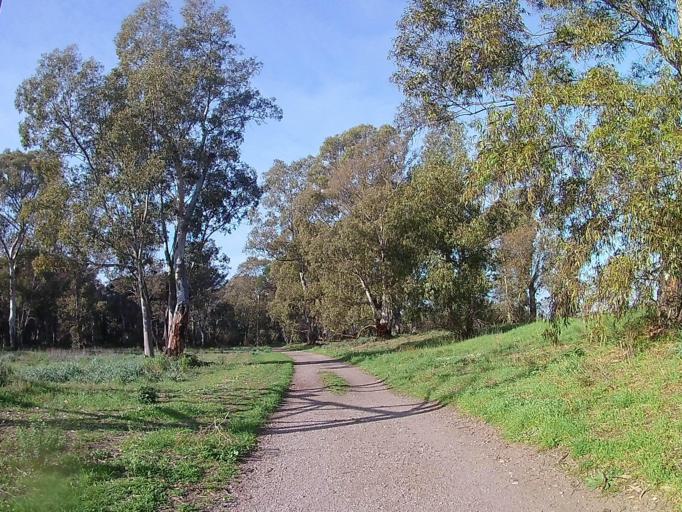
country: IT
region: Latium
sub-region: Citta metropolitana di Roma Capitale
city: Lido di Ostia
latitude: 41.7454
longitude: 12.2822
